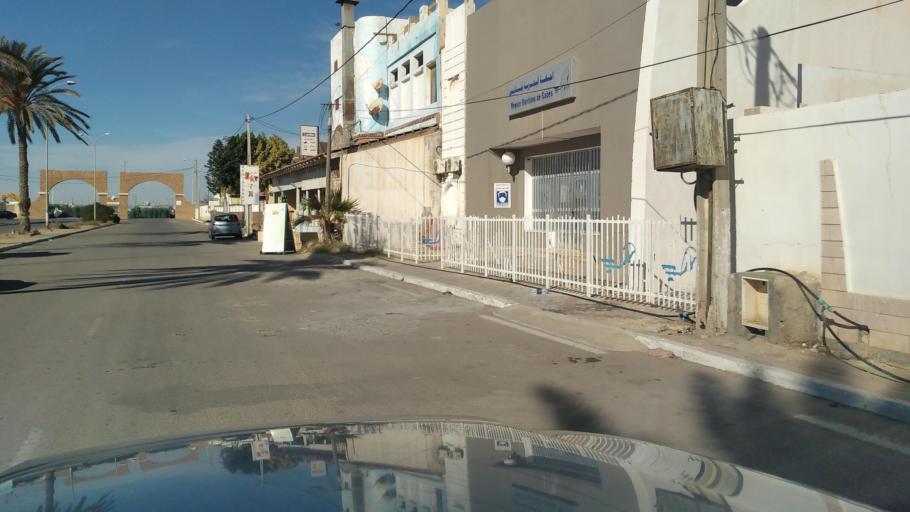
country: TN
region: Qabis
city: Gabes
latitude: 33.8934
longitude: 10.1148
